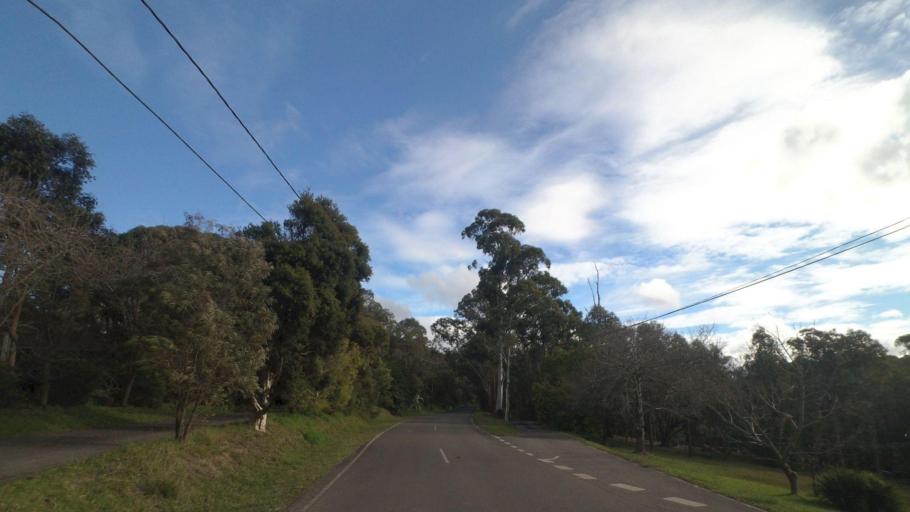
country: AU
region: Victoria
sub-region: Nillumbik
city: North Warrandyte
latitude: -37.7379
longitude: 145.2113
